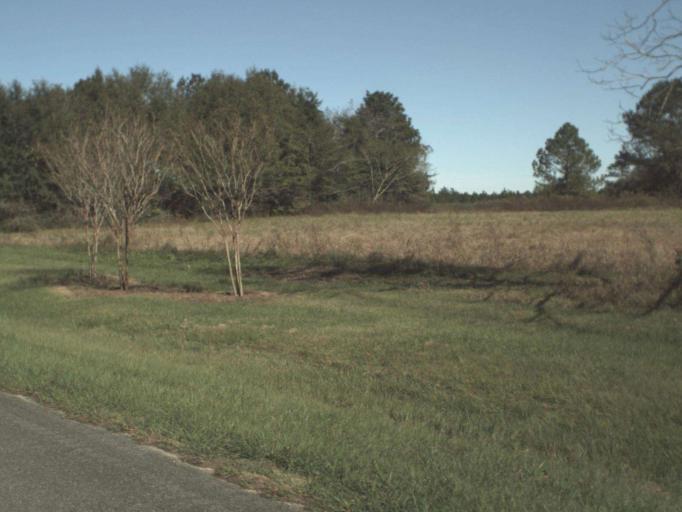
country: US
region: Florida
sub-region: Okaloosa County
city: Crestview
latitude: 30.9894
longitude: -86.6292
